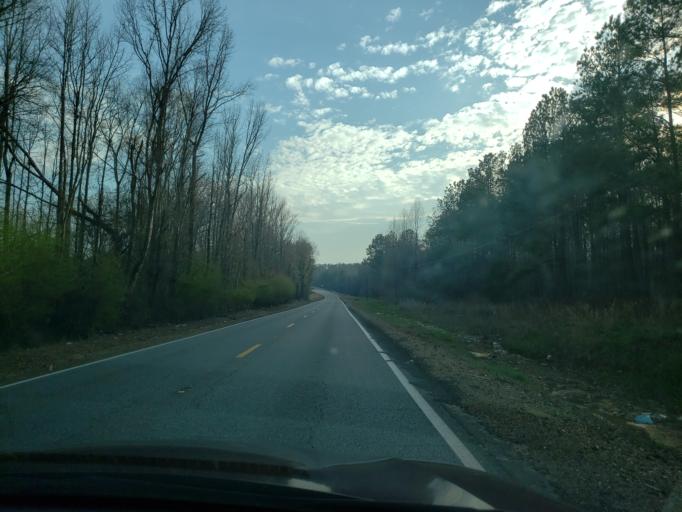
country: US
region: Alabama
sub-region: Hale County
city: Moundville
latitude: 32.9343
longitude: -87.6320
